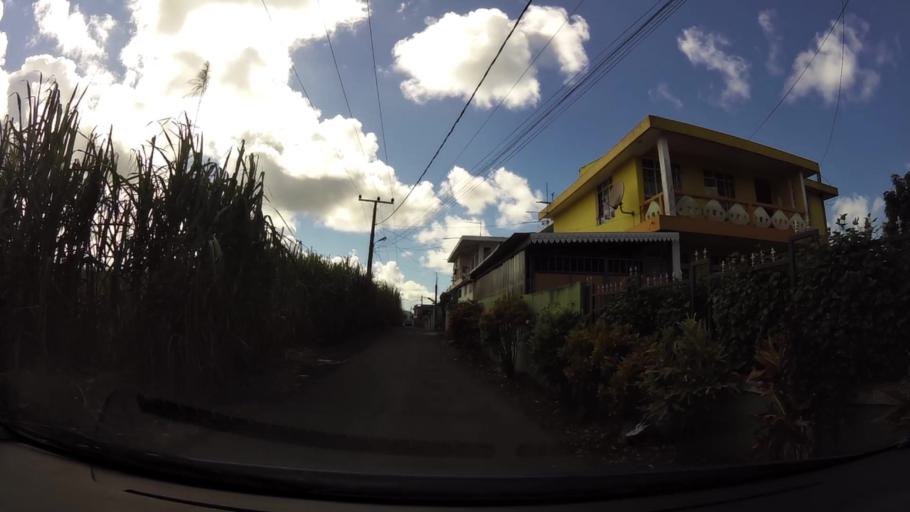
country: MU
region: Grand Port
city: Plaine Magnien
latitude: -20.4293
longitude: 57.6545
